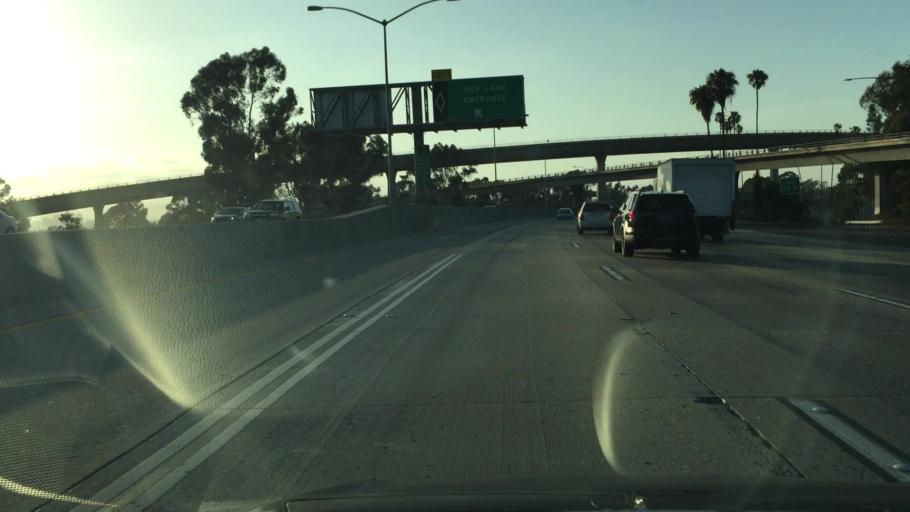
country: US
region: California
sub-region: San Diego County
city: National City
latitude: 32.6879
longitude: -117.0931
